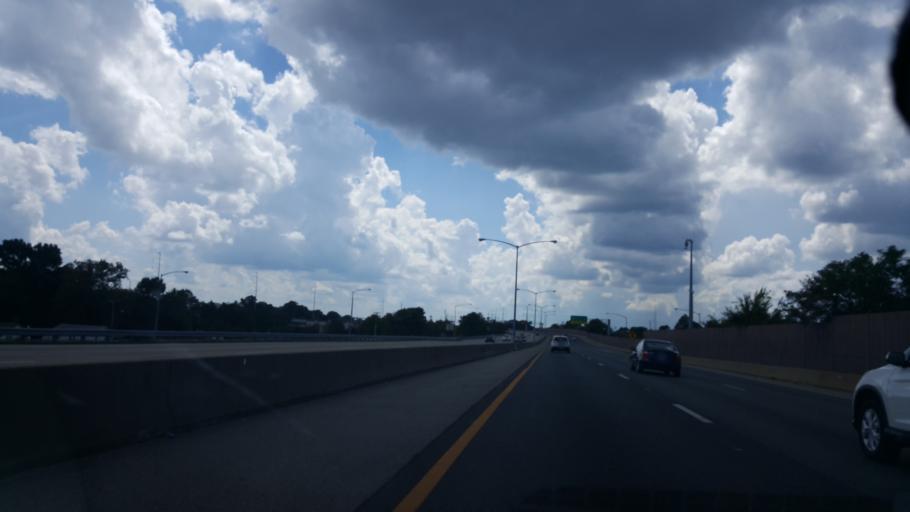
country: US
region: Virginia
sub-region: City of Newport News
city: Newport News
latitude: 36.9958
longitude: -76.4153
